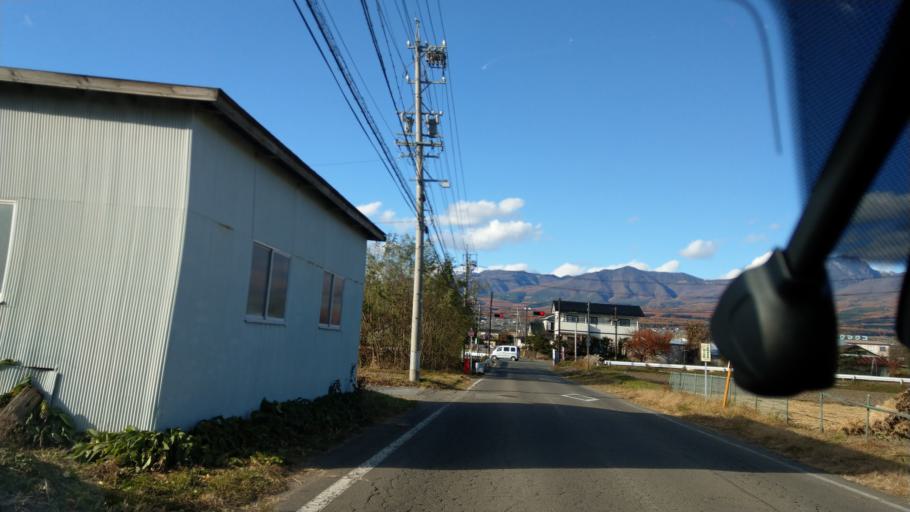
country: JP
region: Nagano
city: Komoro
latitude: 36.3043
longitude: 138.4693
